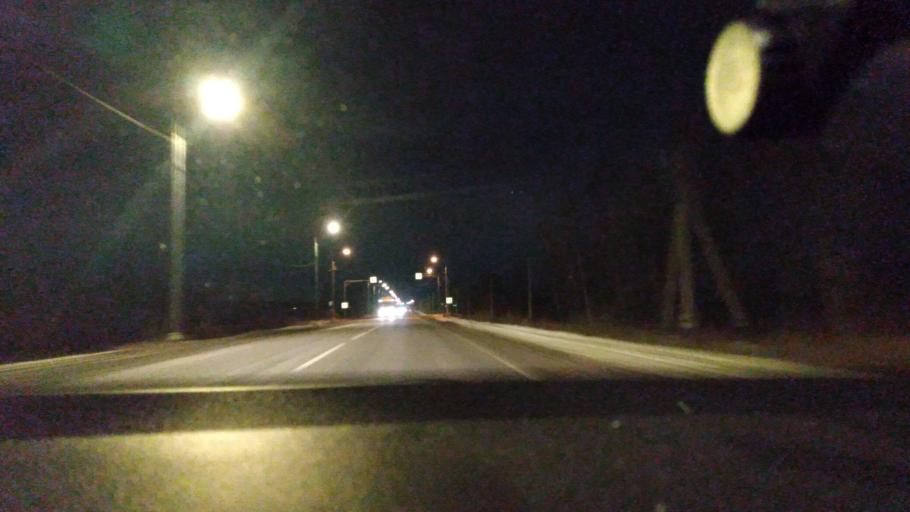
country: RU
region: Moskovskaya
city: Yegor'yevsk
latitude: 55.4100
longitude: 39.0509
